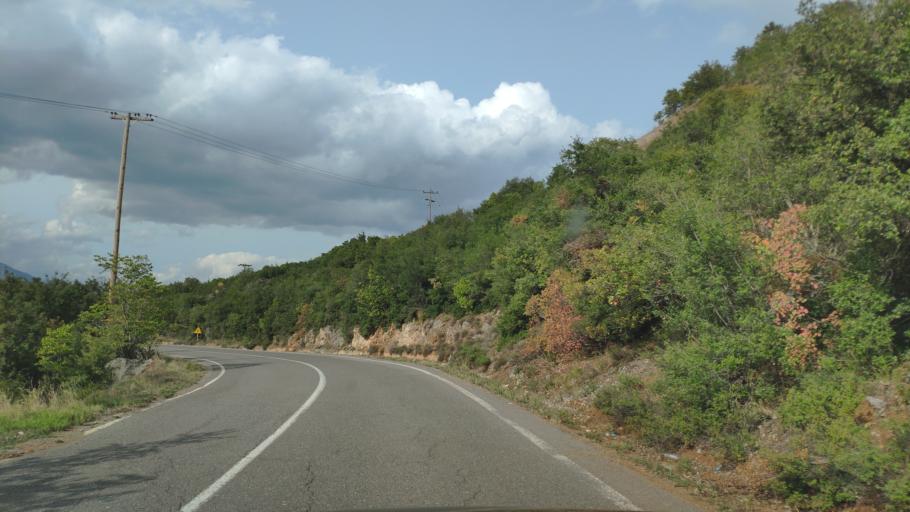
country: GR
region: Central Greece
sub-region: Nomos Fthiotidos
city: Anthili
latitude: 38.7412
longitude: 22.4461
